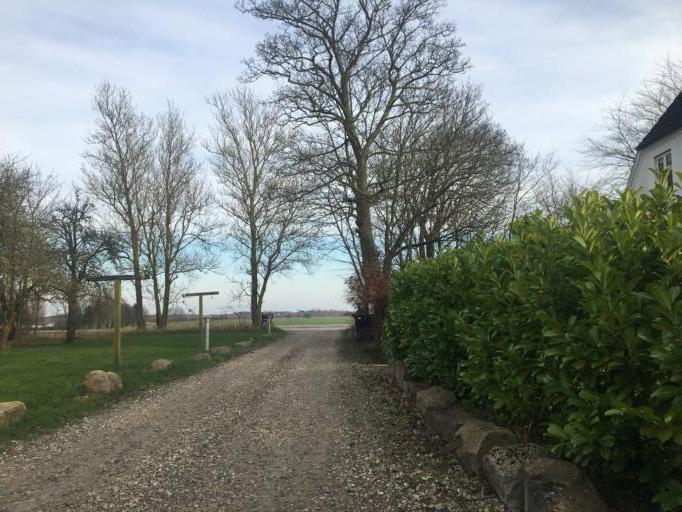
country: DK
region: Zealand
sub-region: Roskilde Kommune
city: Jyllinge
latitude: 55.7405
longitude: 12.1274
